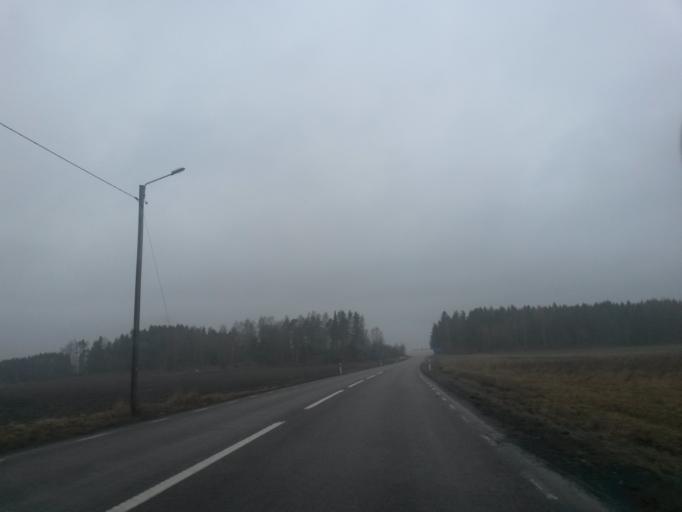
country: SE
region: Vaestra Goetaland
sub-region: Vanersborgs Kommun
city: Vargon
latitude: 58.2573
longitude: 12.4055
